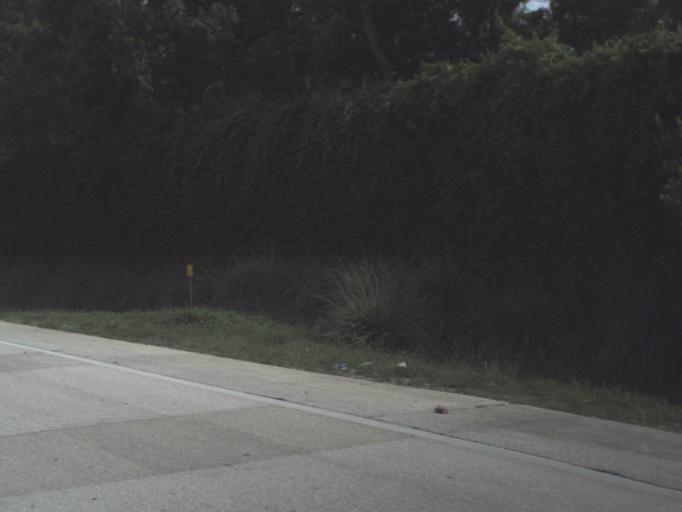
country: US
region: Florida
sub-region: Duval County
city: Jacksonville
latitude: 30.2930
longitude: -81.6321
